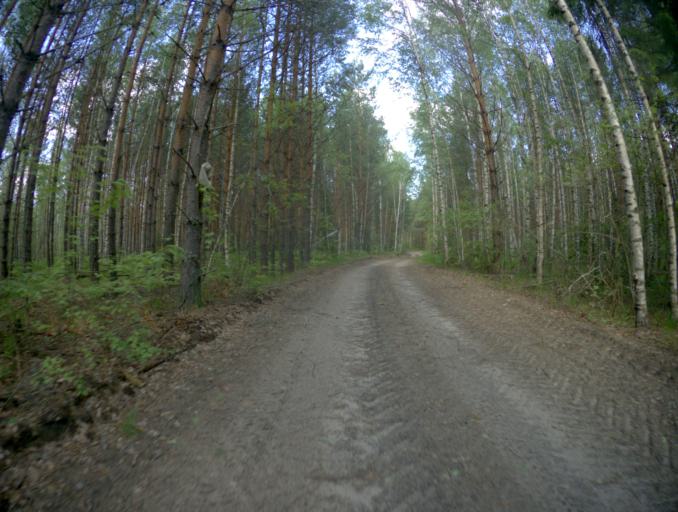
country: RU
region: Vladimir
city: Zolotkovo
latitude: 55.3229
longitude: 40.9346
